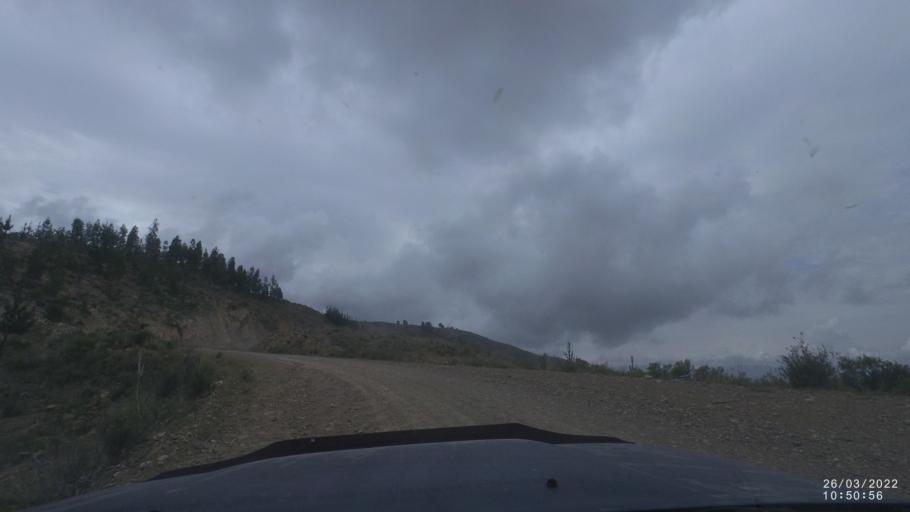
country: BO
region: Cochabamba
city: Tarata
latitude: -17.5115
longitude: -66.0288
